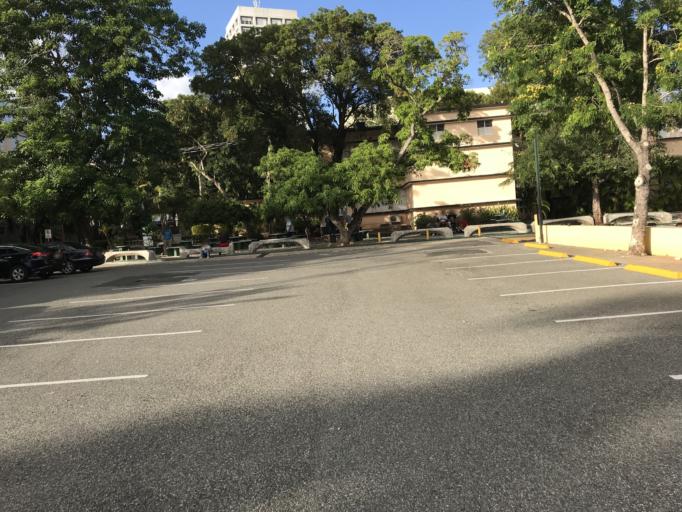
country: DO
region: Nacional
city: La Julia
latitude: 18.4628
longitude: -69.9230
